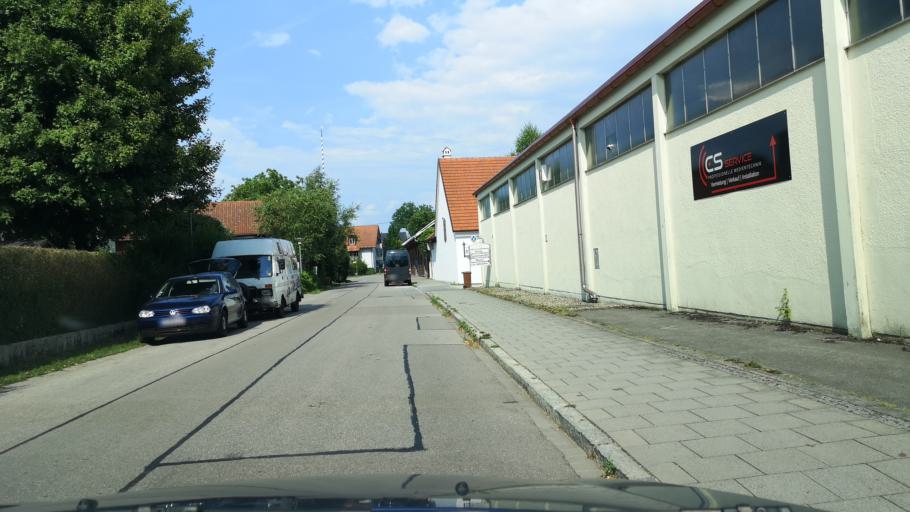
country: DE
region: Bavaria
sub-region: Upper Bavaria
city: Kirchheim bei Muenchen
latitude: 48.1760
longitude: 11.7420
